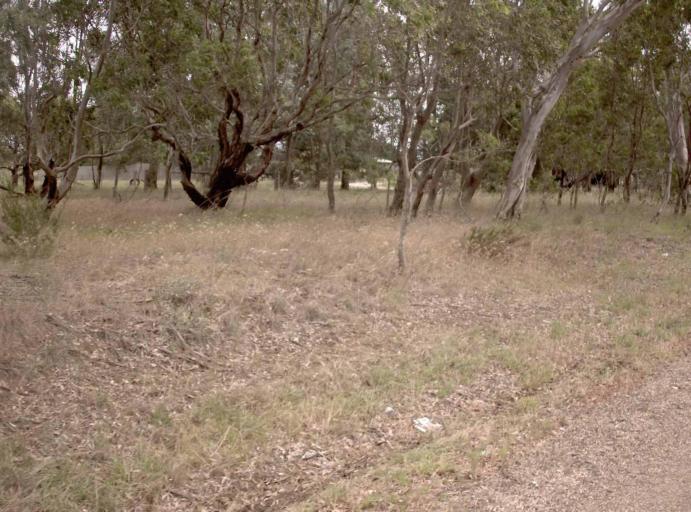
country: AU
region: Victoria
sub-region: Wellington
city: Sale
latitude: -37.9400
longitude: 147.0934
